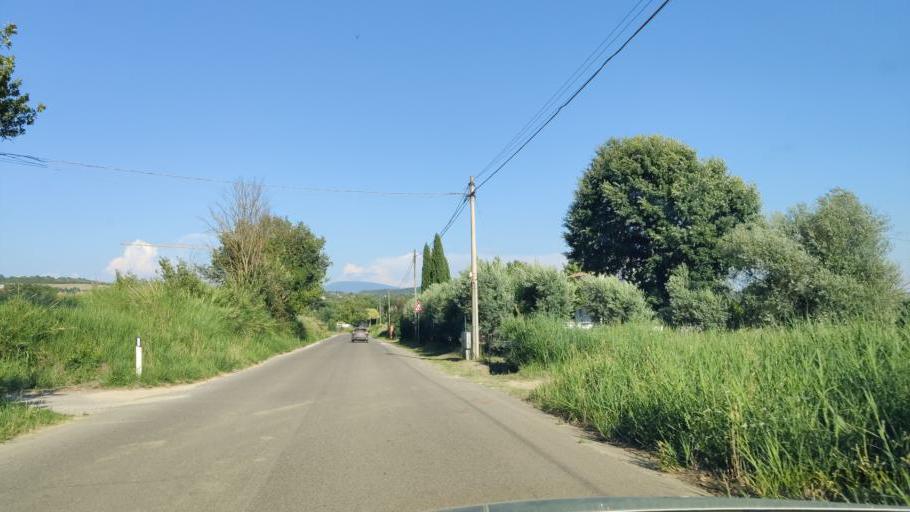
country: IT
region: Latium
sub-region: Provincia di Viterbo
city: Orte
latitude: 42.4690
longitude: 12.3864
